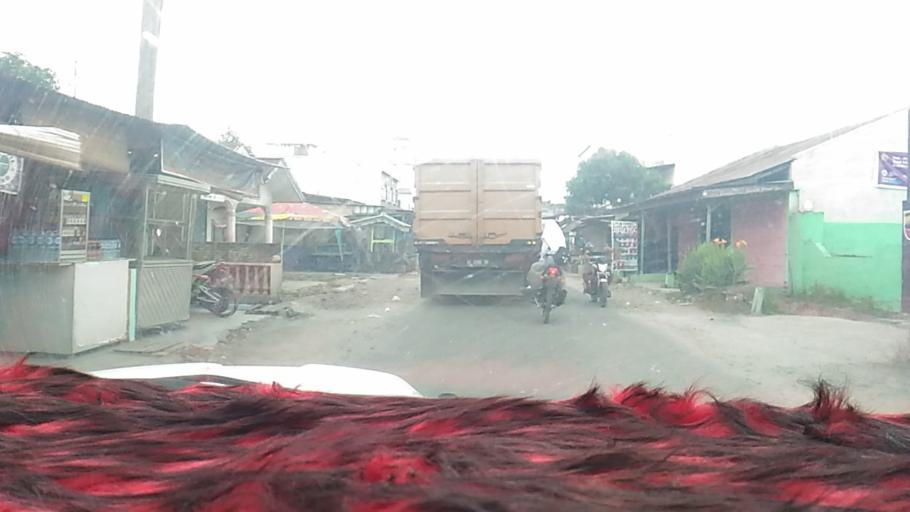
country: ID
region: North Sumatra
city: Binjai
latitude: 3.5977
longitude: 98.5519
